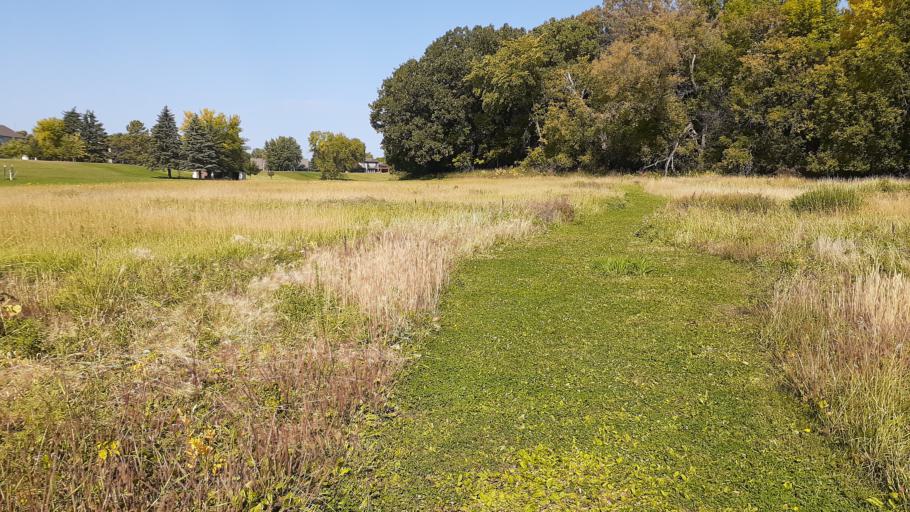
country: US
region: Minnesota
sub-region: Clay County
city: Oakport
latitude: 46.9105
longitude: -96.7649
